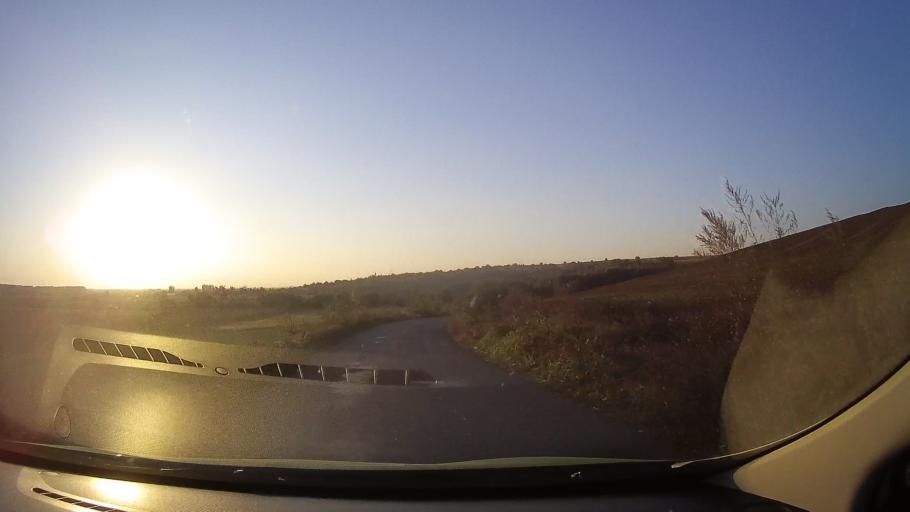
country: RO
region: Bihor
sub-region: Comuna Salard
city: Salard
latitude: 47.2490
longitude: 22.0164
